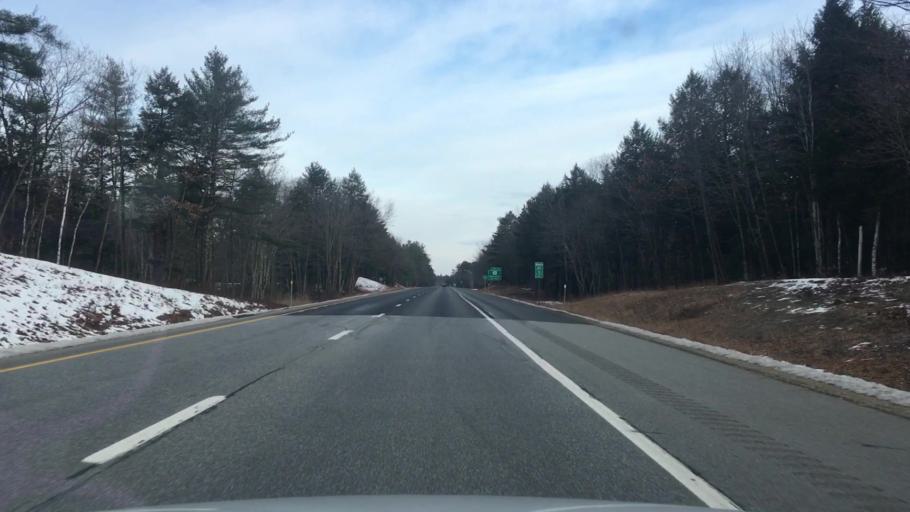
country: US
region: New Hampshire
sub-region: Merrimack County
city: Contoocook
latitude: 43.2386
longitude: -71.7454
